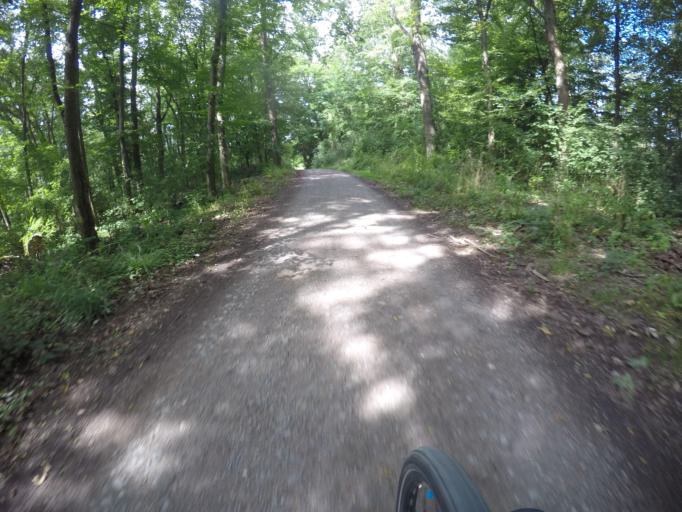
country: DE
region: Baden-Wuerttemberg
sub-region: Karlsruhe Region
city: Otisheim
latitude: 48.9798
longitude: 8.7877
